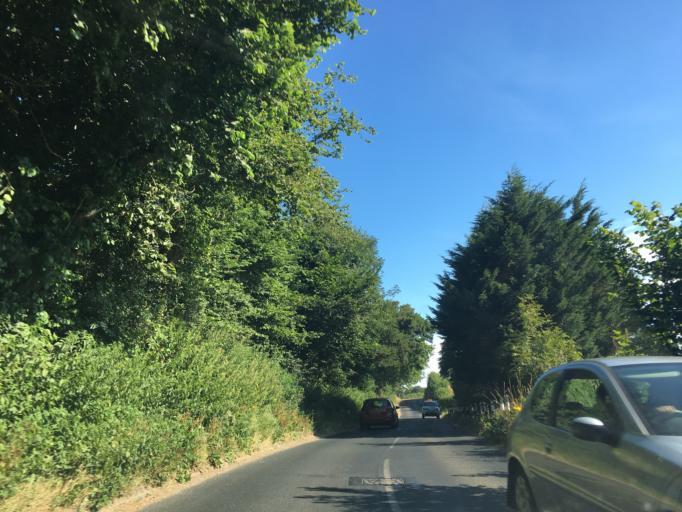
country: GB
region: England
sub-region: Isle of Wight
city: Newport
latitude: 50.6829
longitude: -1.3116
